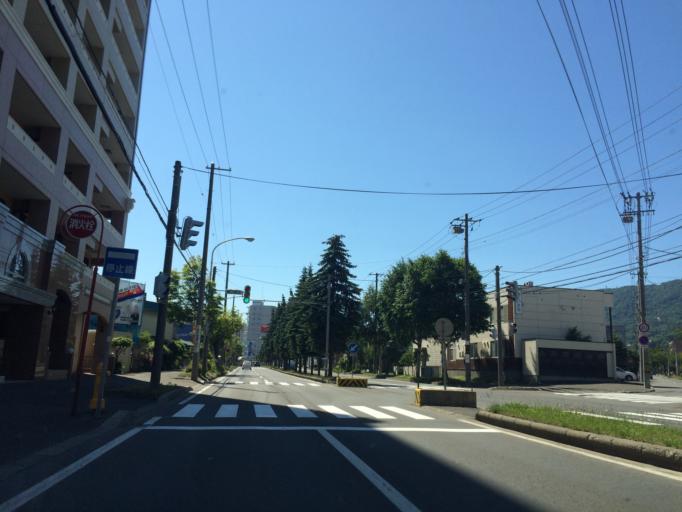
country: JP
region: Hokkaido
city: Sapporo
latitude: 43.0486
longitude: 141.3206
